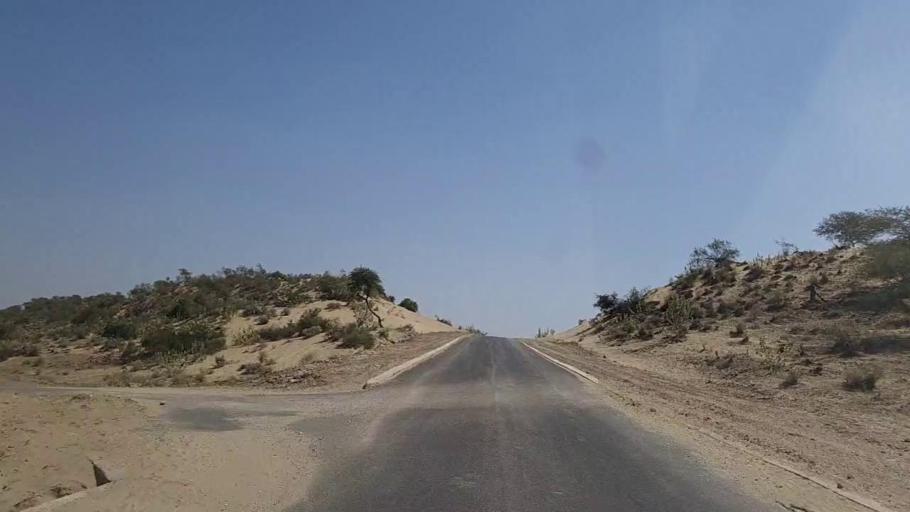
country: PK
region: Sindh
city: Diplo
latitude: 24.4825
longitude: 69.4786
